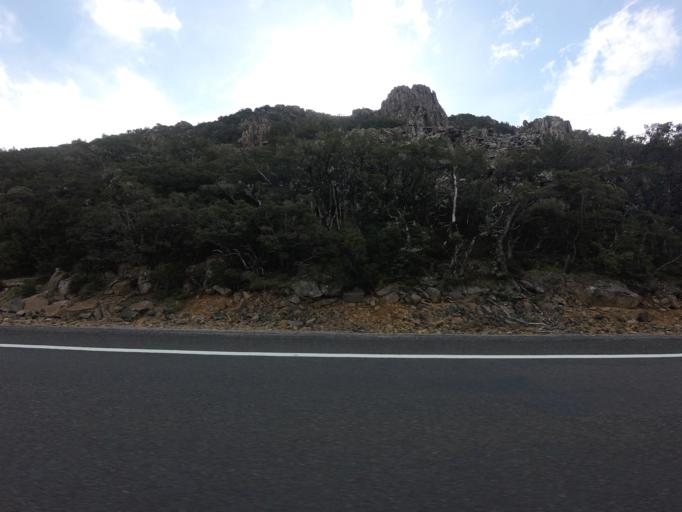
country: AU
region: Tasmania
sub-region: Meander Valley
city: Deloraine
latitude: -41.7301
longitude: 146.7183
